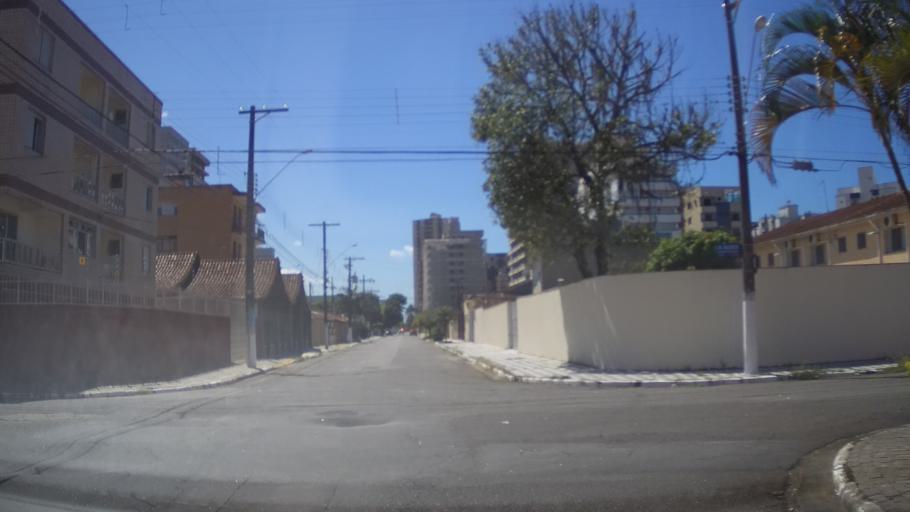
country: BR
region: Sao Paulo
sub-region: Mongagua
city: Mongagua
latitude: -24.0507
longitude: -46.5324
